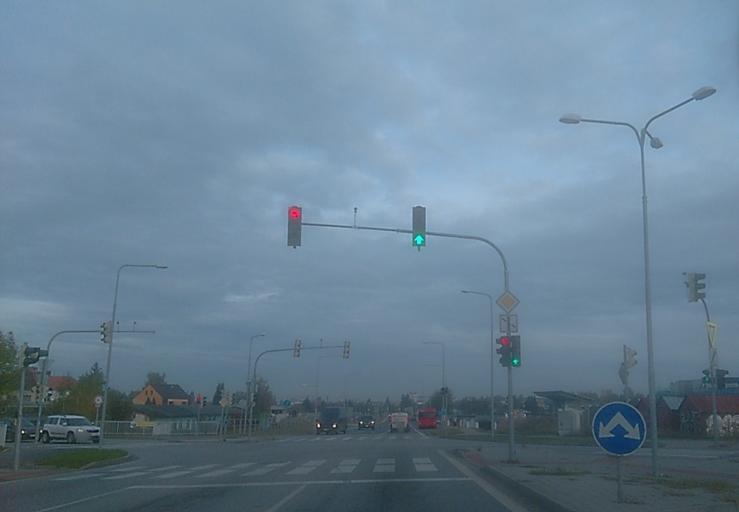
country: CZ
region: Jihocesky
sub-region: Okres Ceske Budejovice
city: Ceske Budejovice
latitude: 48.9816
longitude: 14.4882
